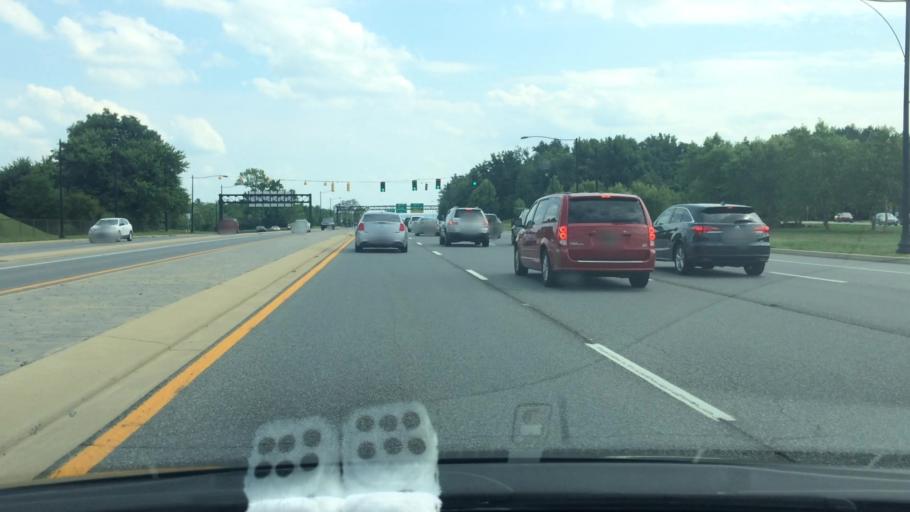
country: US
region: Delaware
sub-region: New Castle County
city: Wilmington
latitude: 39.7728
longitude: -75.5441
